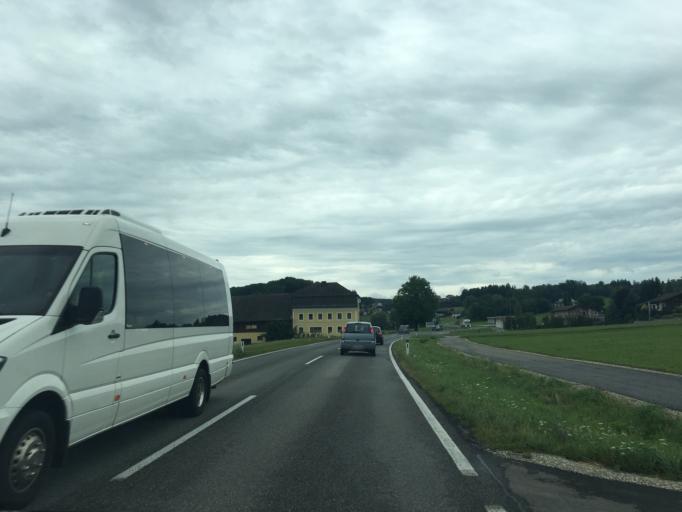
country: AT
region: Salzburg
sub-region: Politischer Bezirk Salzburg-Umgebung
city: Dorfbeuern
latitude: 48.0618
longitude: 12.9874
